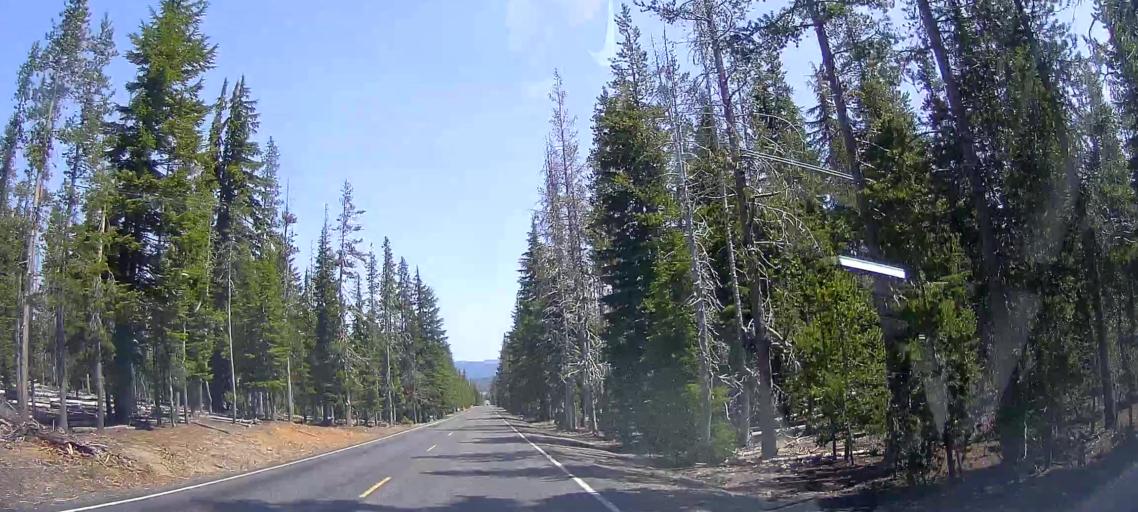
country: US
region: Oregon
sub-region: Jackson County
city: Shady Cove
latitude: 43.0095
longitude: -122.1310
